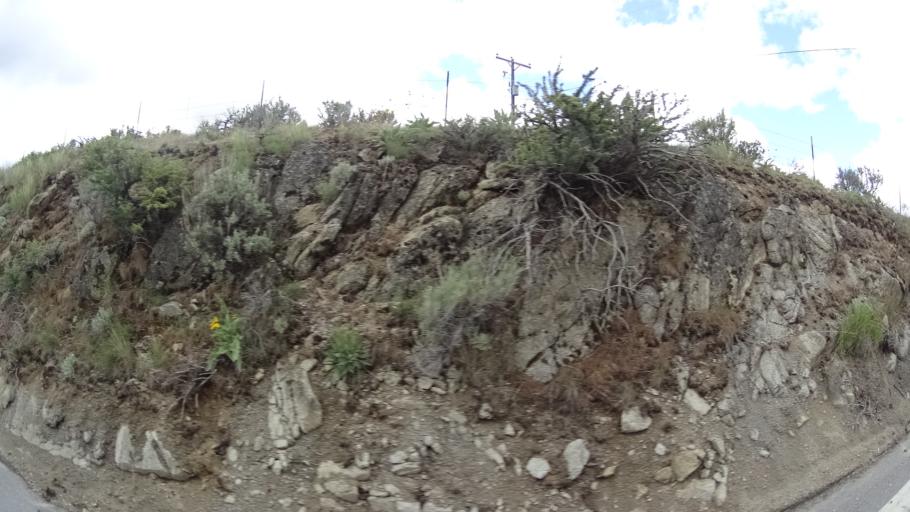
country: US
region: Idaho
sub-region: Ada County
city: Boise
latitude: 43.7132
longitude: -116.1637
